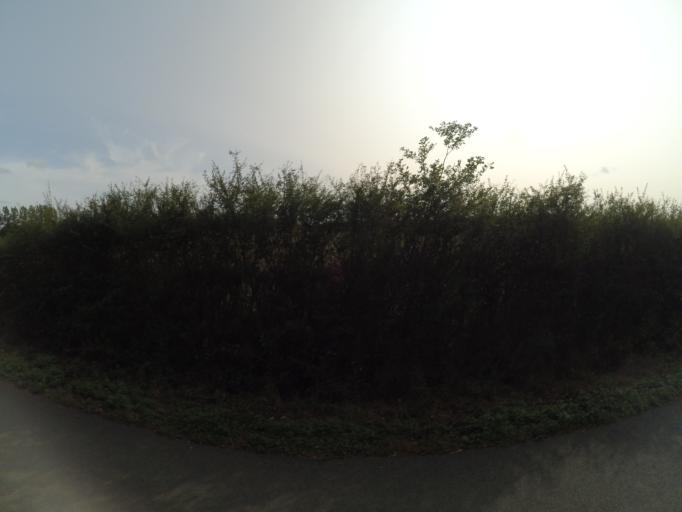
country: FR
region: Pays de la Loire
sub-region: Departement de la Vendee
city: Saint-Hilaire-de-Loulay
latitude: 46.9845
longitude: -1.3358
